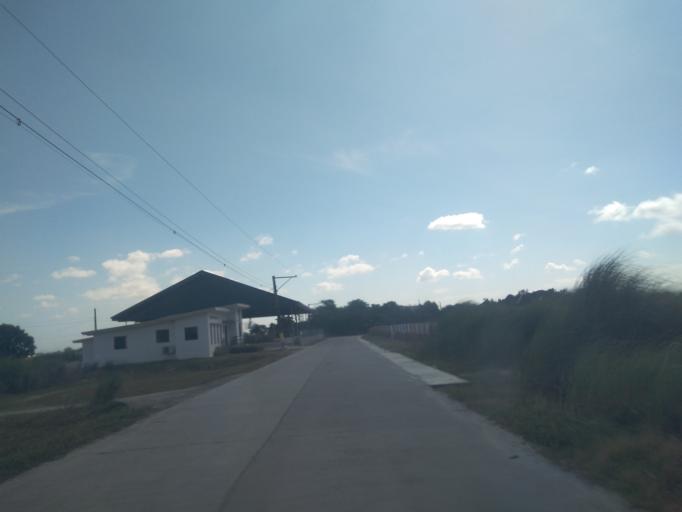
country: PH
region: Central Luzon
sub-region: Province of Pampanga
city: Balas
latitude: 15.0520
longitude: 120.6097
